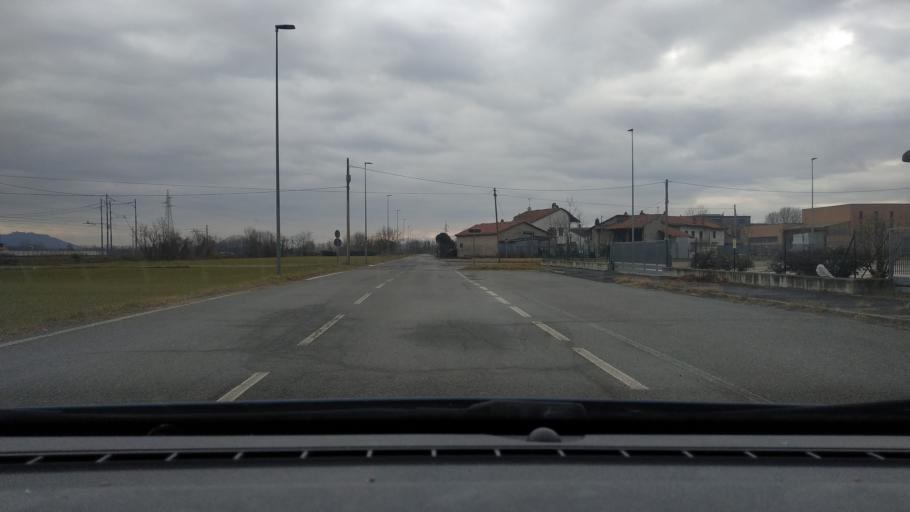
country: IT
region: Piedmont
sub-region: Provincia di Torino
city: Ivrea
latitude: 45.4352
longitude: 7.8895
